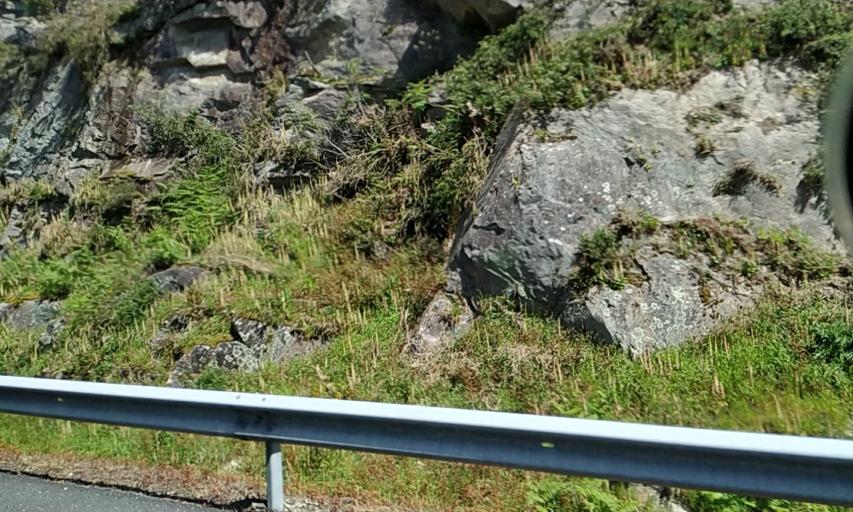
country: ES
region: Galicia
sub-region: Provincia da Coruna
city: Padron
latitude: 42.7402
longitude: -8.6435
